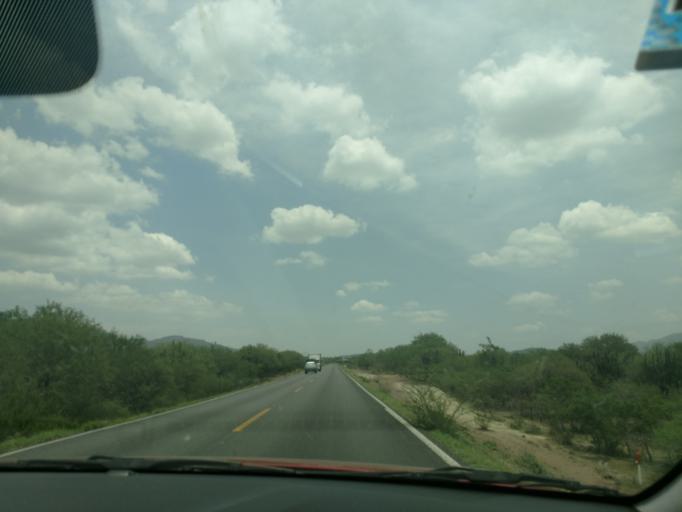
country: MX
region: San Luis Potosi
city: Villa Juarez
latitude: 22.0185
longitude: -100.3926
